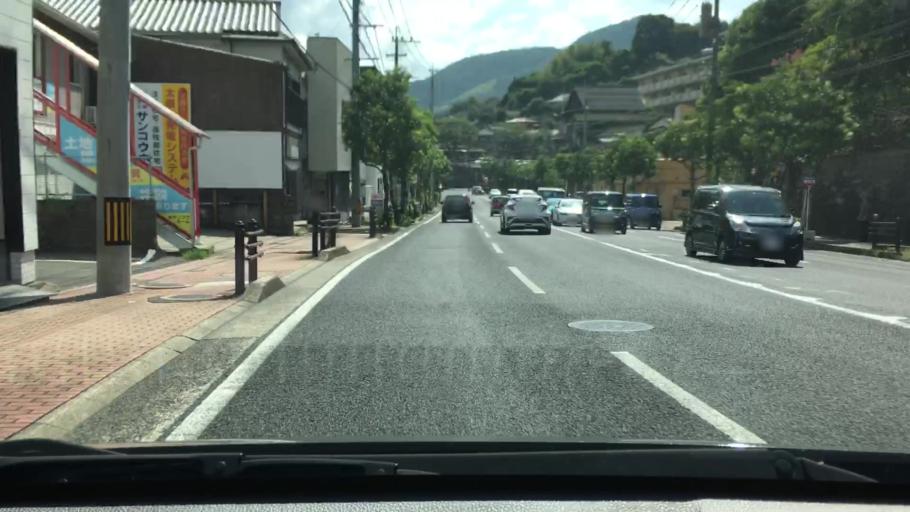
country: JP
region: Nagasaki
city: Sasebo
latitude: 33.1960
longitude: 129.7219
